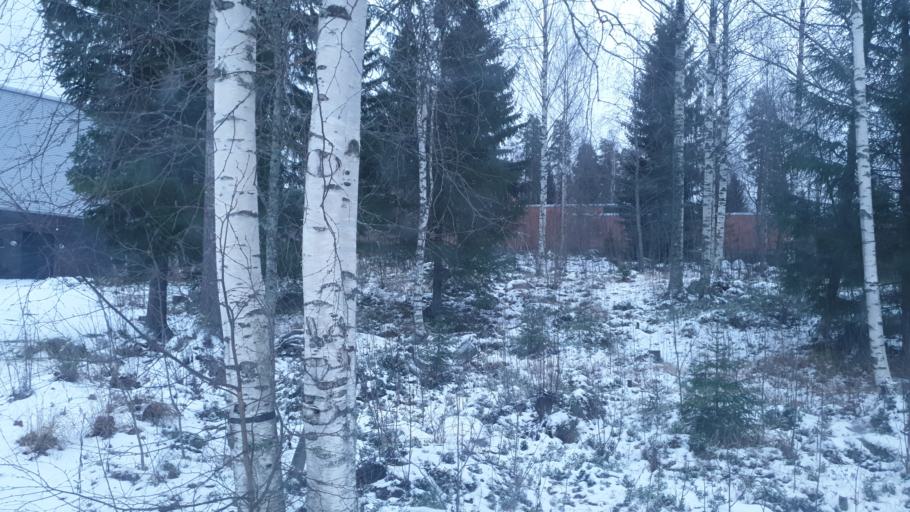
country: FI
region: Northern Savo
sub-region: Kuopio
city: Kuopio
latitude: 62.8381
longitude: 27.6423
